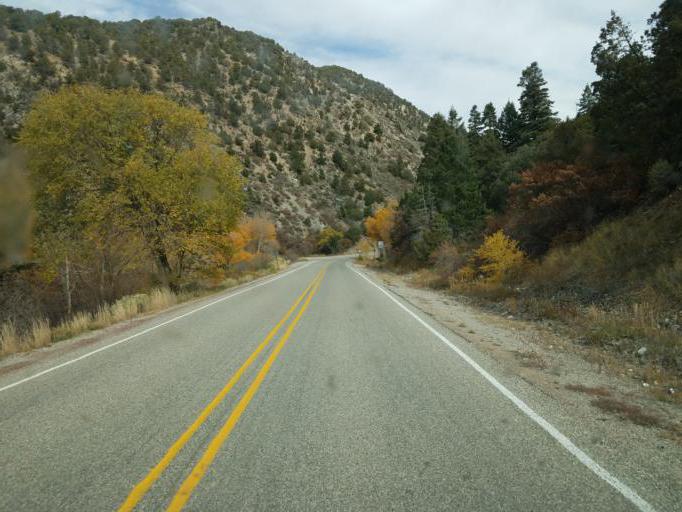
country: US
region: New Mexico
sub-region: Taos County
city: Arroyo Seco
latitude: 36.5406
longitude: -105.5605
